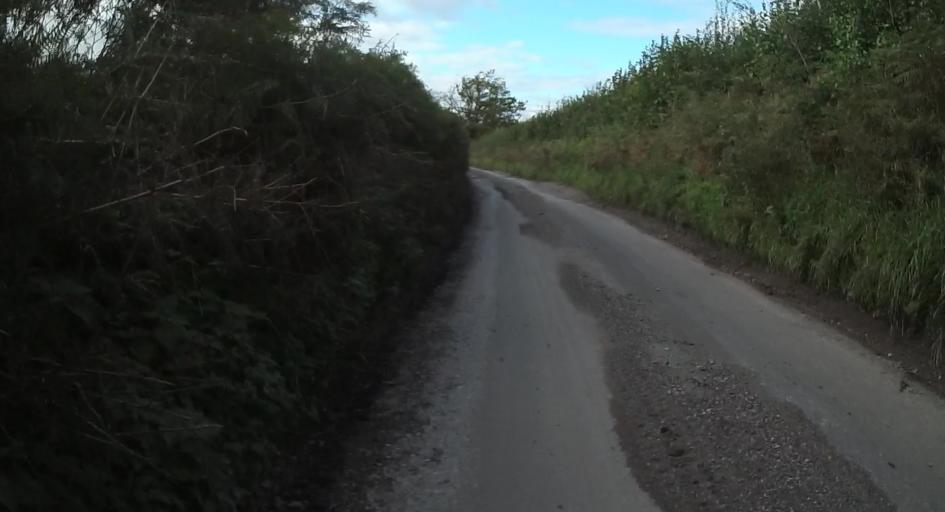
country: GB
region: England
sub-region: Hampshire
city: Kingsley
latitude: 51.1529
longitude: -0.9219
